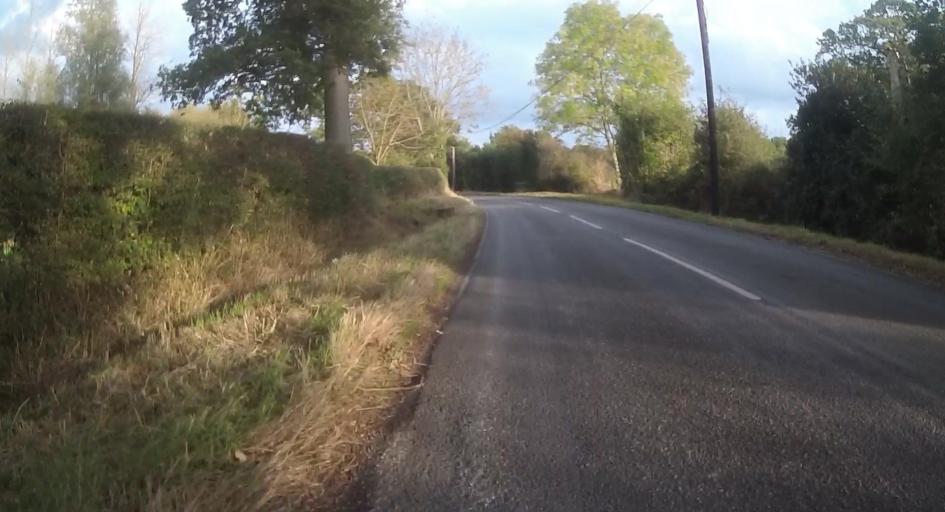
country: GB
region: England
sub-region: Hampshire
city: Tadley
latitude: 51.3802
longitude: -1.1712
